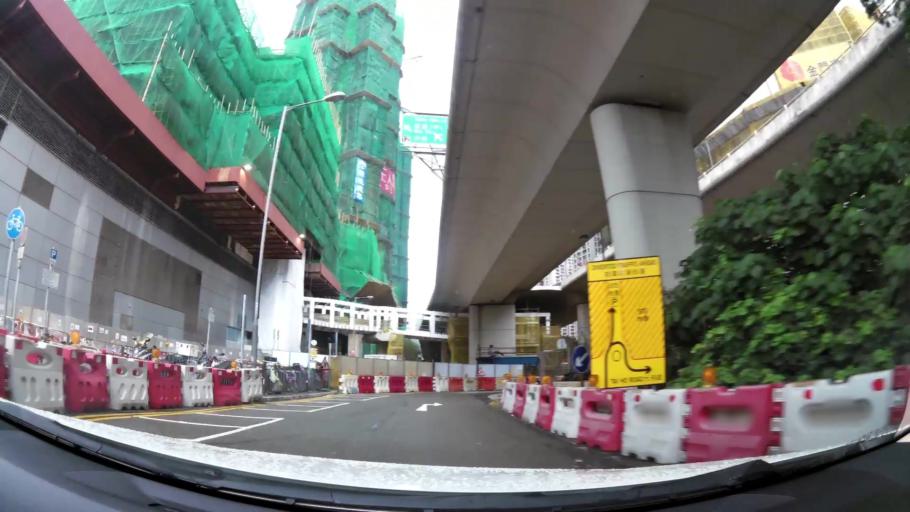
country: HK
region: Tsuen Wan
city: Tsuen Wan
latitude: 22.3677
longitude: 114.1113
